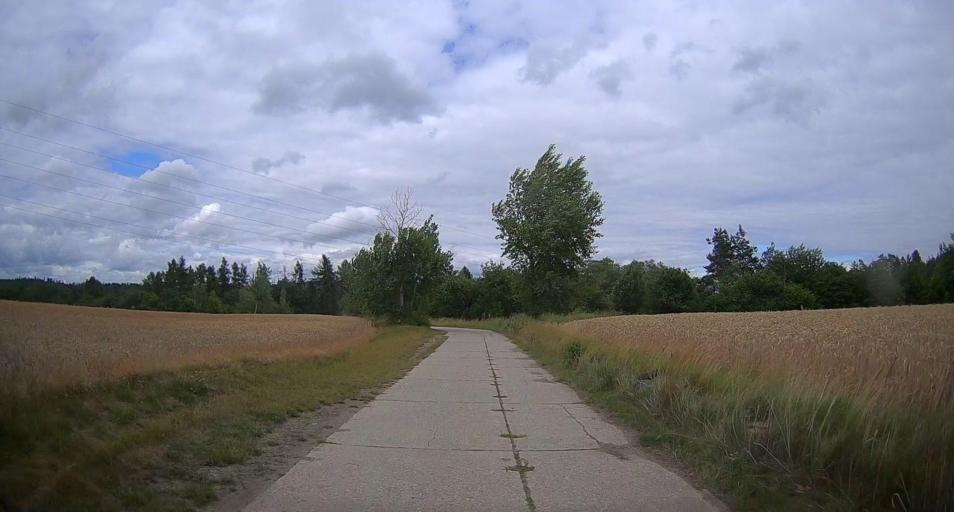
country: CZ
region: South Moravian
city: Lipuvka
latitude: 49.3292
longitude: 16.5370
